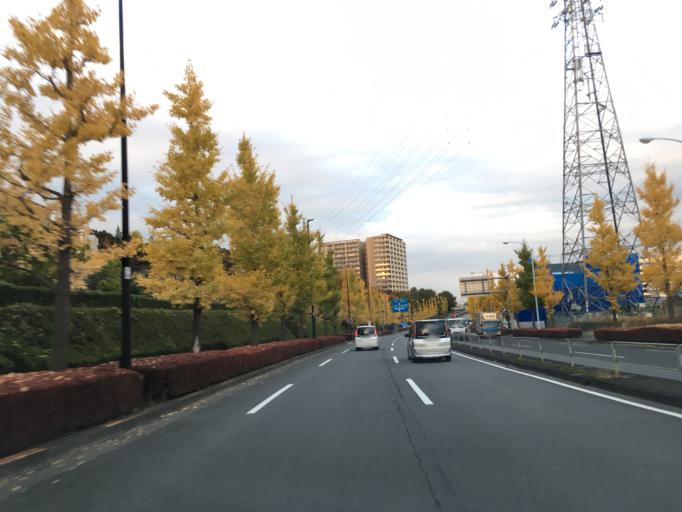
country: JP
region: Tokyo
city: Hachioji
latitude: 35.6112
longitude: 139.3736
